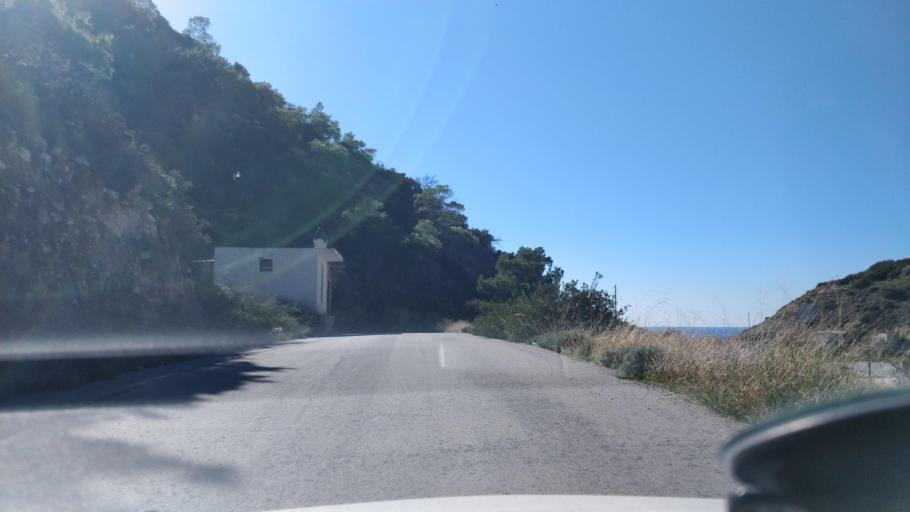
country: GR
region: Crete
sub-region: Nomos Lasithiou
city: Gra Liyia
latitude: 34.9898
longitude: 25.4846
